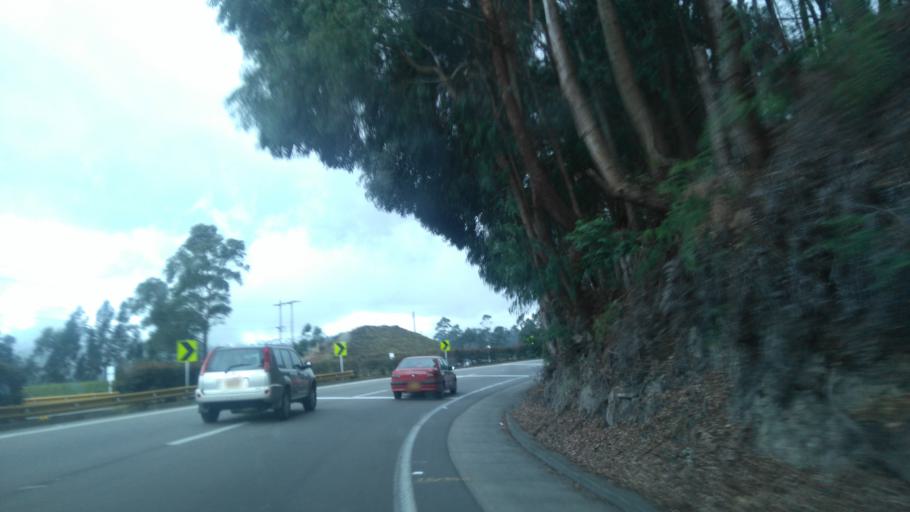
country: CO
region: Cundinamarca
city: El Rosal
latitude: 4.8888
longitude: -74.3011
